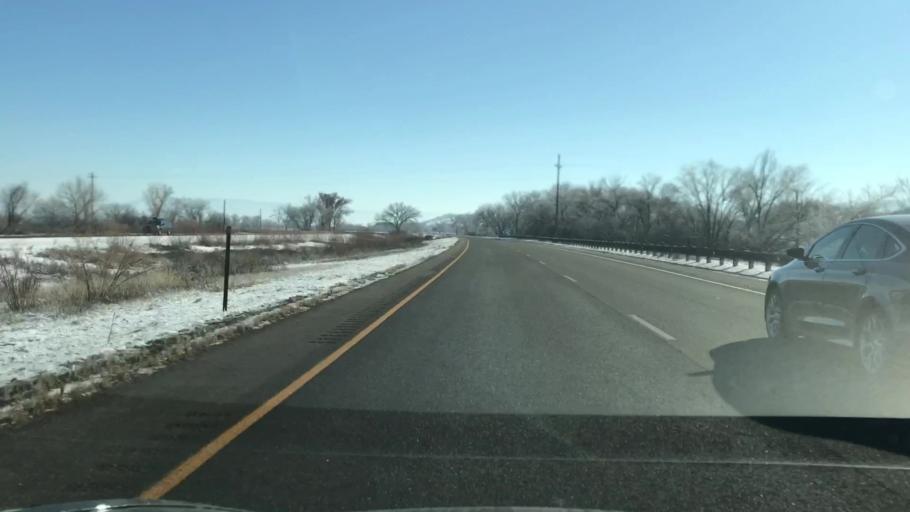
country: US
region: Colorado
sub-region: Mesa County
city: Loma
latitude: 39.1667
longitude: -108.7881
